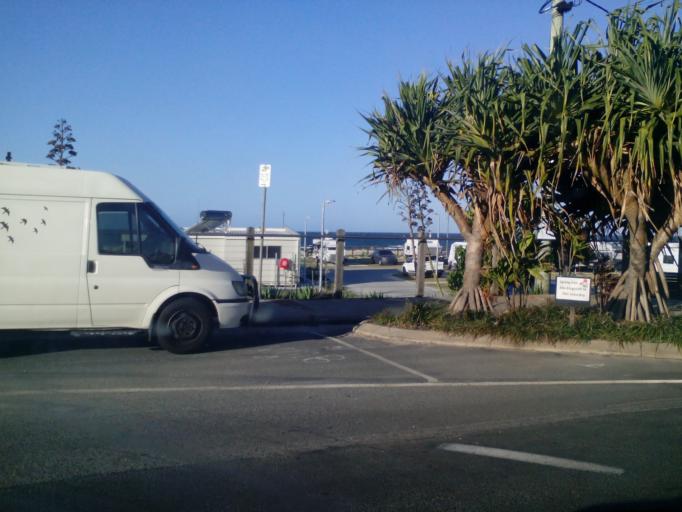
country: AU
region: New South Wales
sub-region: Tweed
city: Kingscliff
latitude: -28.2546
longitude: 153.5753
